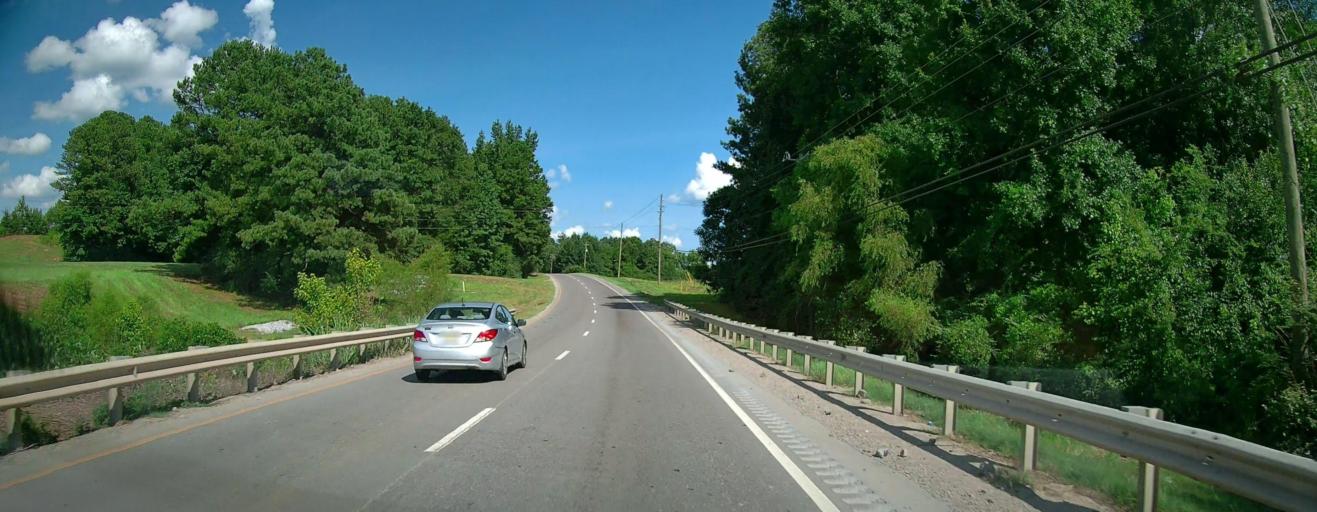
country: US
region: Alabama
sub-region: Tuscaloosa County
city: Northport
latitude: 33.2372
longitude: -87.6551
